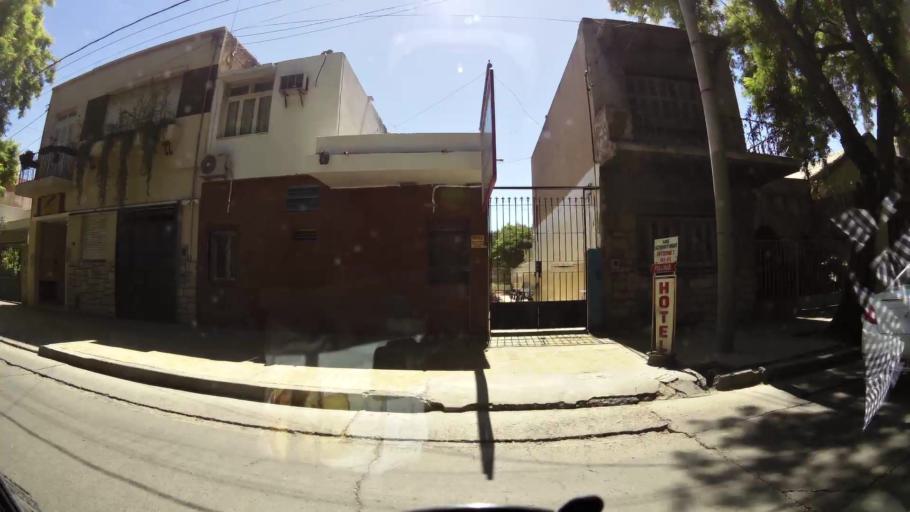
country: AR
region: San Juan
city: San Juan
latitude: -31.5350
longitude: -68.5199
